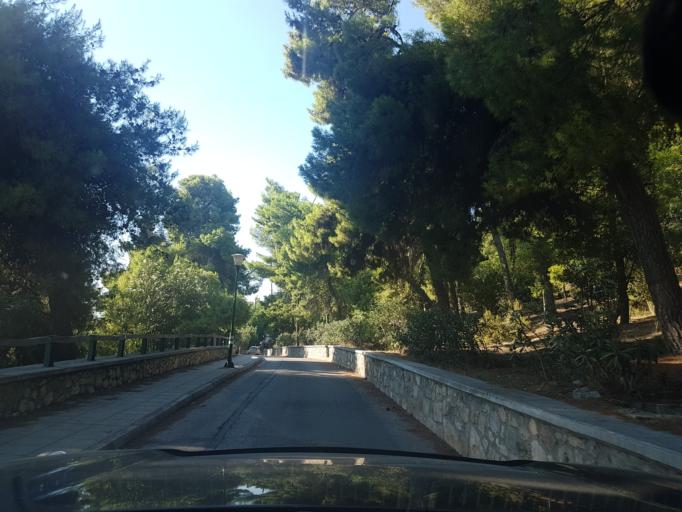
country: GR
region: Central Greece
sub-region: Nomos Evvoias
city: Chalkida
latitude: 38.4665
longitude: 23.5873
